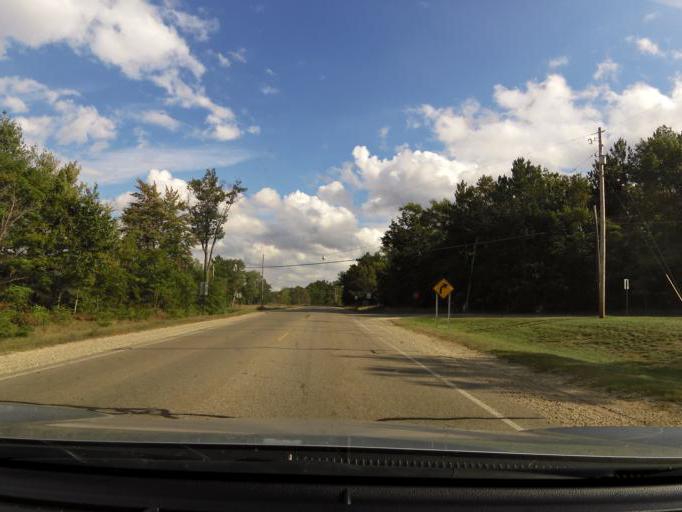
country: US
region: Michigan
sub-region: Roscommon County
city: Saint Helen
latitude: 44.3758
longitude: -84.4142
